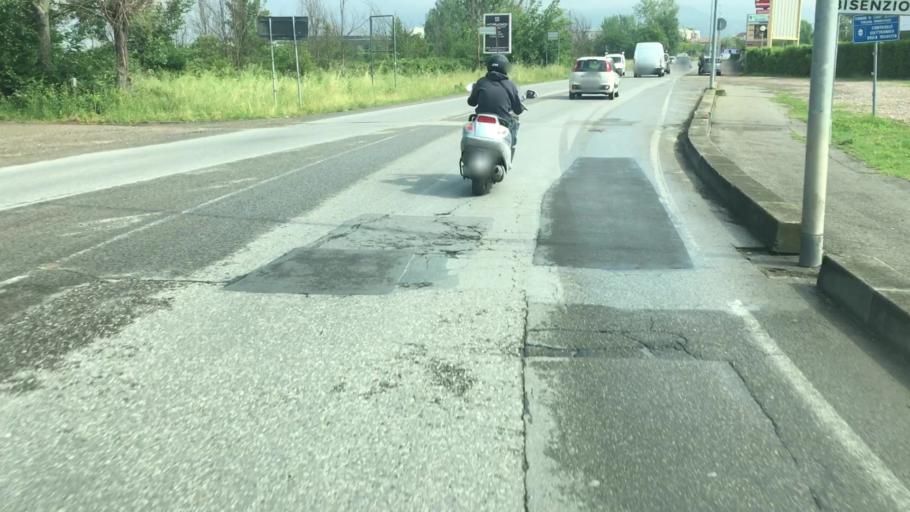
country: IT
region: Tuscany
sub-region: Province of Florence
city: Campi Bisenzio
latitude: 43.8166
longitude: 11.1211
